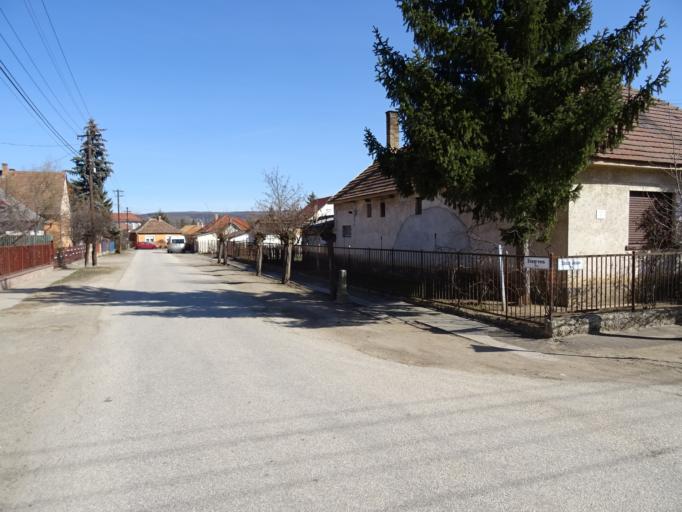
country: HU
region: Pest
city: Veresegyhaz
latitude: 47.6434
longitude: 19.2811
